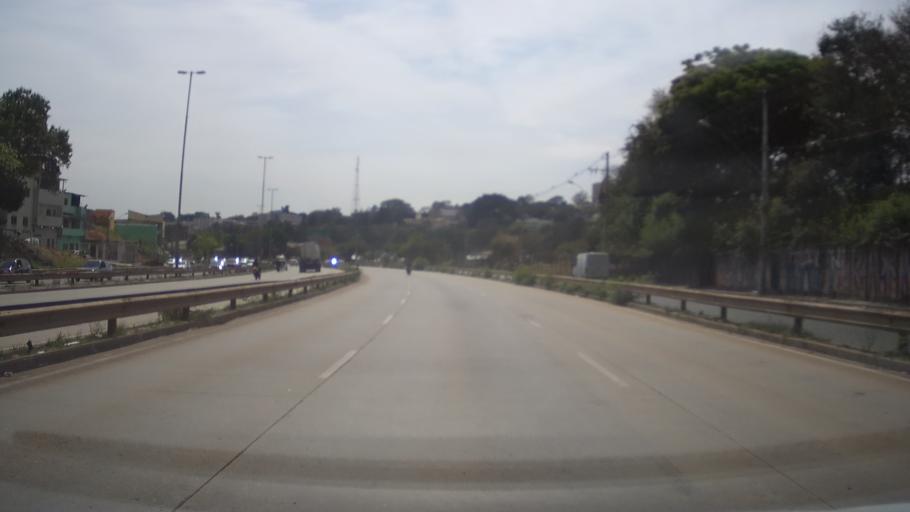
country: BR
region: Minas Gerais
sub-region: Contagem
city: Contagem
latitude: -19.9363
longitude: -43.9999
